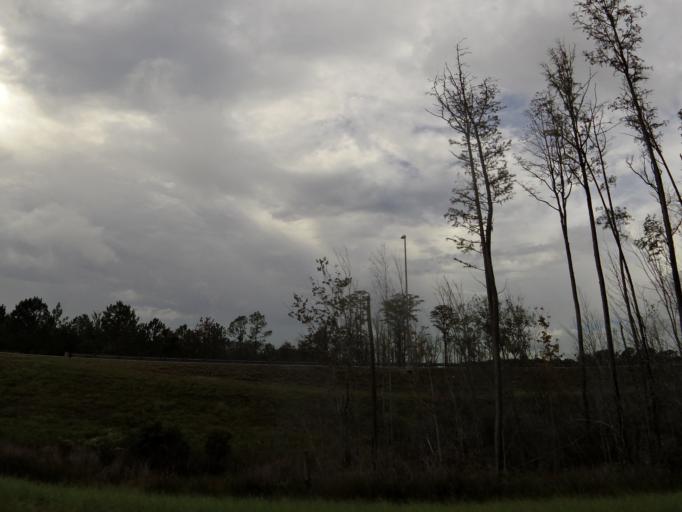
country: US
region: Florida
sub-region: Duval County
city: Baldwin
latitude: 30.3049
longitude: -81.8826
